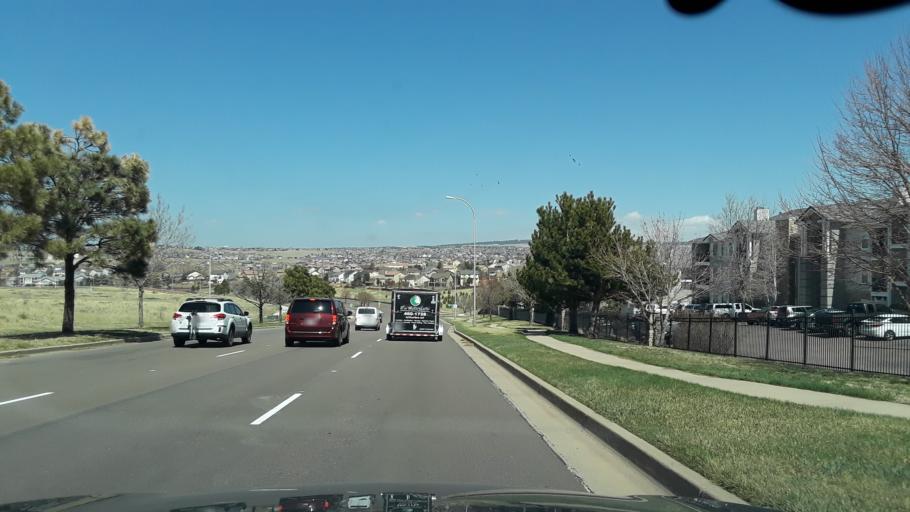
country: US
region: Colorado
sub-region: El Paso County
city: Cimarron Hills
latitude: 38.9234
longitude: -104.7384
